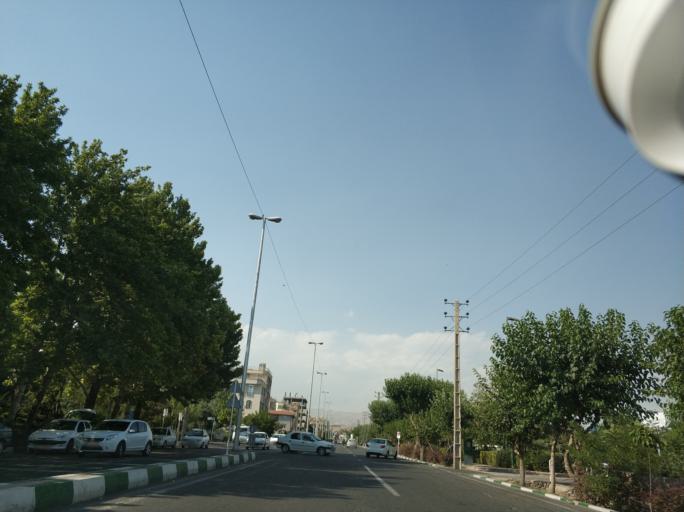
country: IR
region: Tehran
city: Tajrish
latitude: 35.7555
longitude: 51.5391
